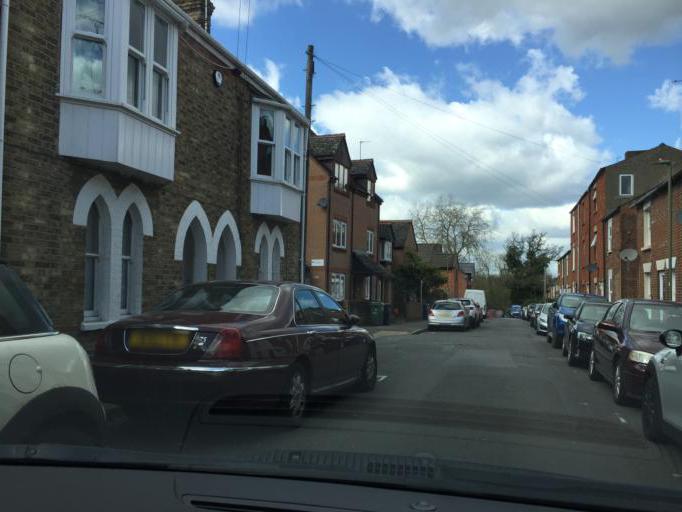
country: GB
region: England
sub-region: Oxfordshire
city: Oxford
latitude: 51.7522
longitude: -1.2376
